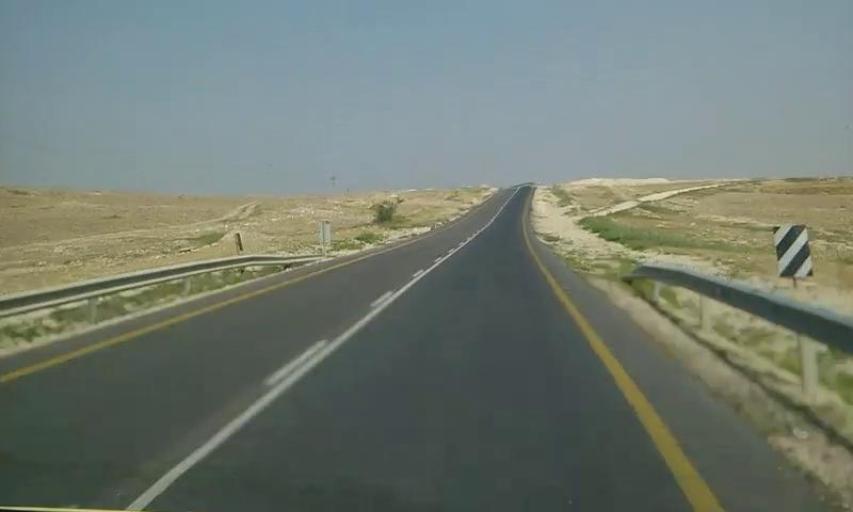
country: PS
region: West Bank
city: Al `Awja
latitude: 31.9696
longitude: 35.4705
